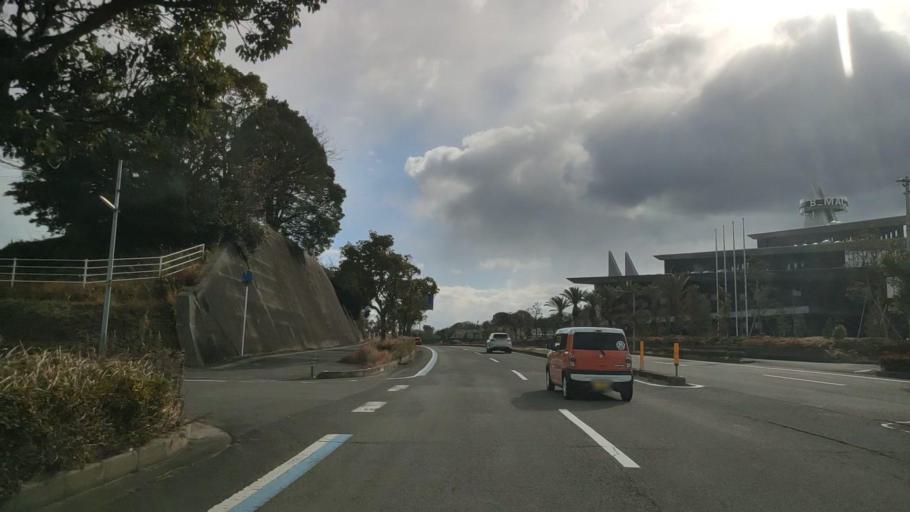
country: JP
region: Ehime
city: Hojo
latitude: 34.0643
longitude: 132.9529
